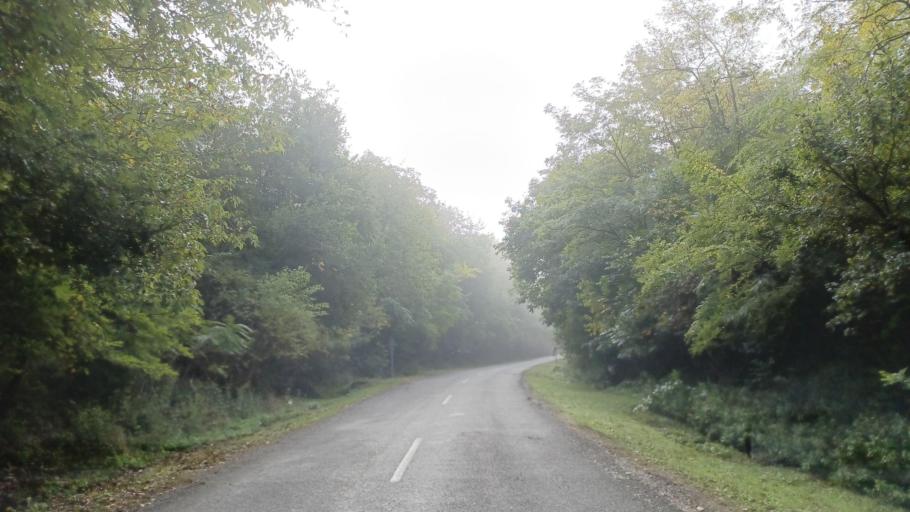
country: HU
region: Tolna
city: Pincehely
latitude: 46.6801
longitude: 18.4652
